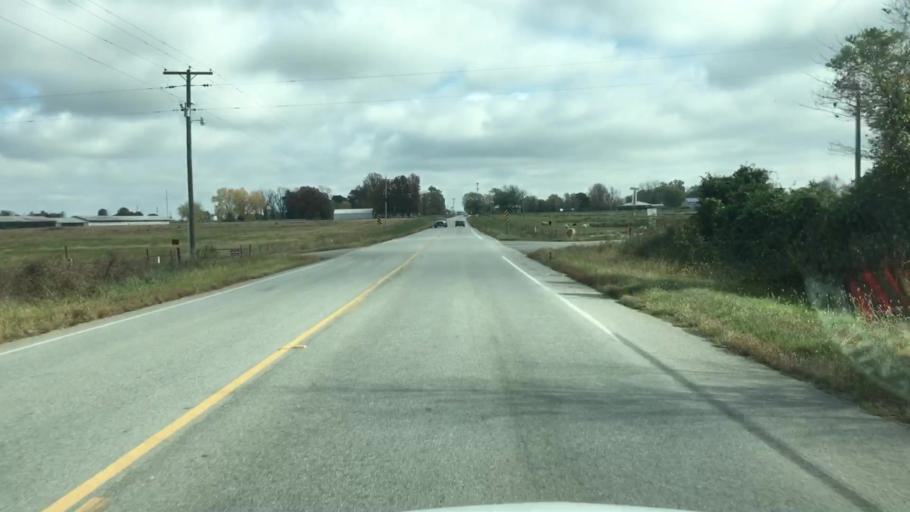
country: US
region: Arkansas
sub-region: Benton County
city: Gentry
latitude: 36.2618
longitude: -94.3643
